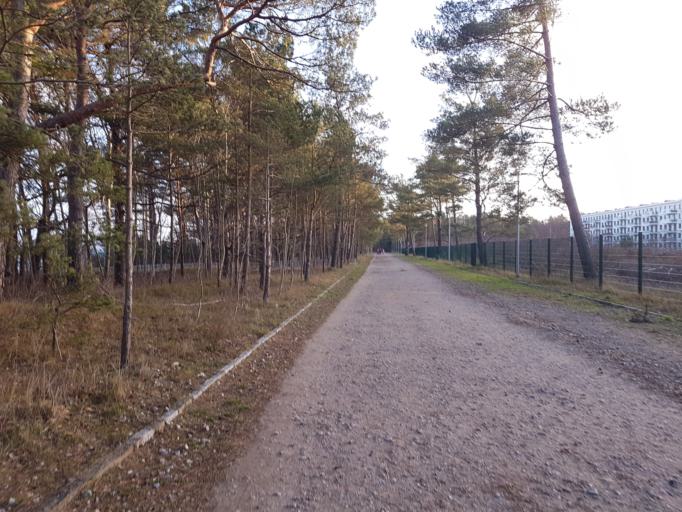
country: DE
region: Mecklenburg-Vorpommern
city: Ostseebad Binz
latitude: 54.4291
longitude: 13.5837
